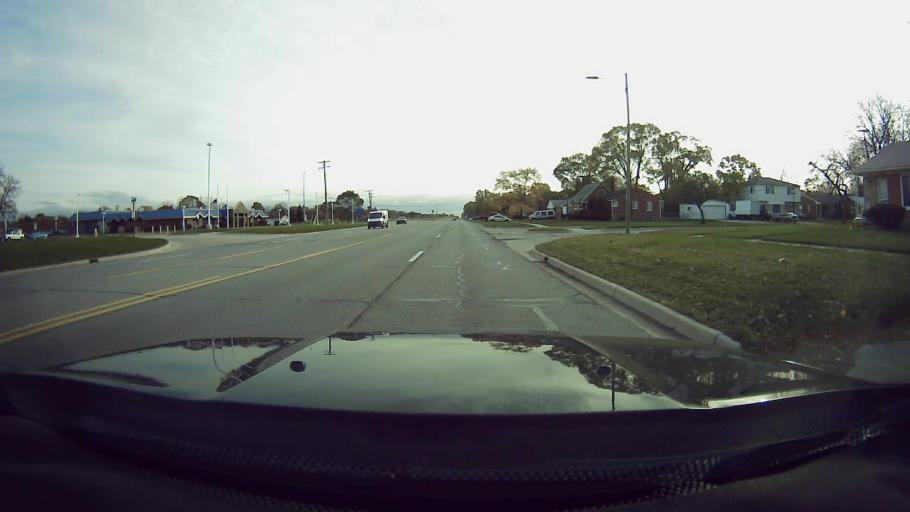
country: US
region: Michigan
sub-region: Oakland County
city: Oak Park
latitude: 42.4739
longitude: -83.1918
